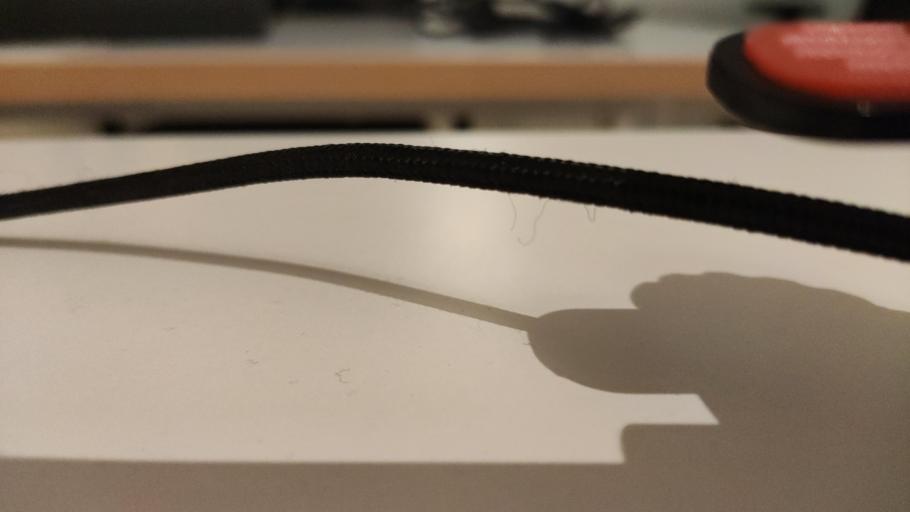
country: RU
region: Moskovskaya
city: Budenovetc
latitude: 56.3790
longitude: 37.5972
